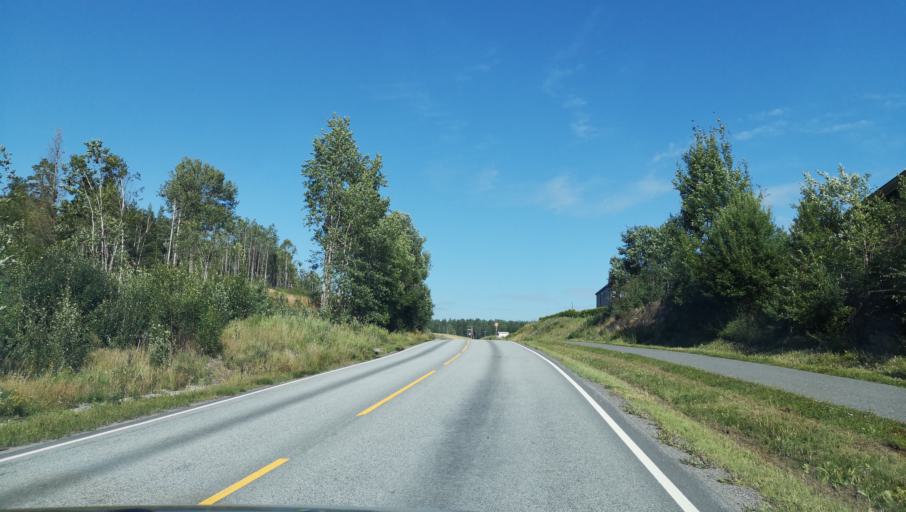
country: NO
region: Ostfold
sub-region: Valer
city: Kirkebygda
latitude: 59.5596
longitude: 10.8471
